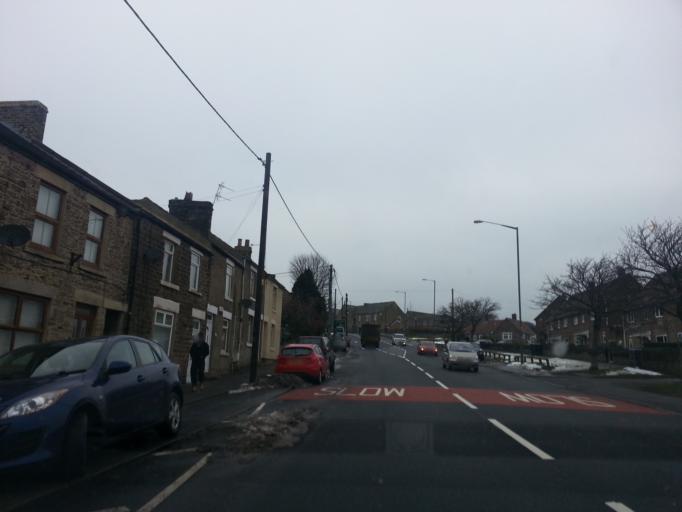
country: GB
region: England
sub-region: County Durham
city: Tow Law
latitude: 54.7470
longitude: -1.8149
